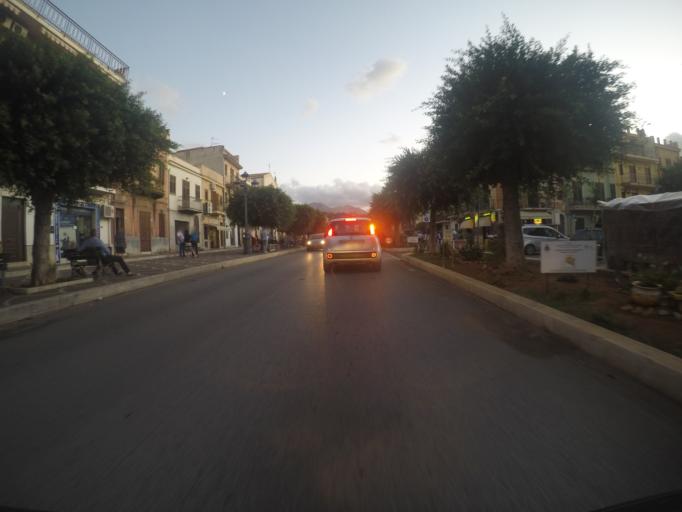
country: IT
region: Sicily
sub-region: Palermo
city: Capaci
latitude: 38.1725
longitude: 13.2402
